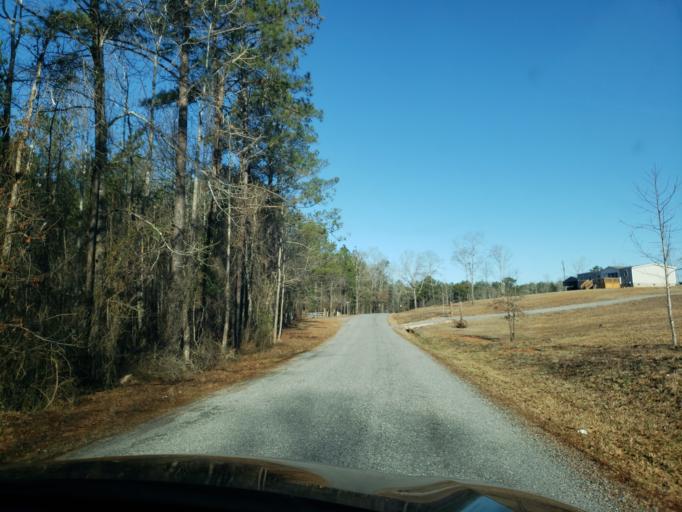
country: US
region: Alabama
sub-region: Elmore County
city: Tallassee
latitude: 32.6679
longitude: -85.8756
